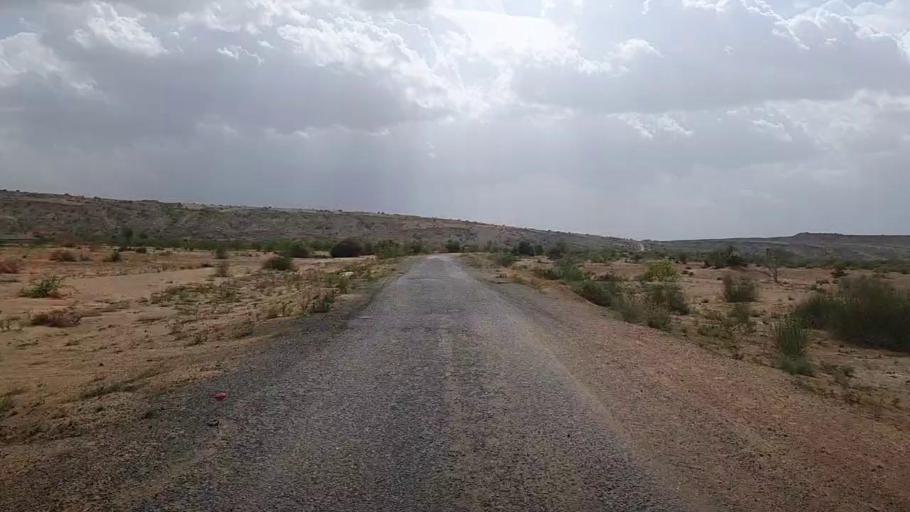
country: PK
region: Sindh
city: Jamshoro
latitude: 25.3941
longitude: 67.7503
